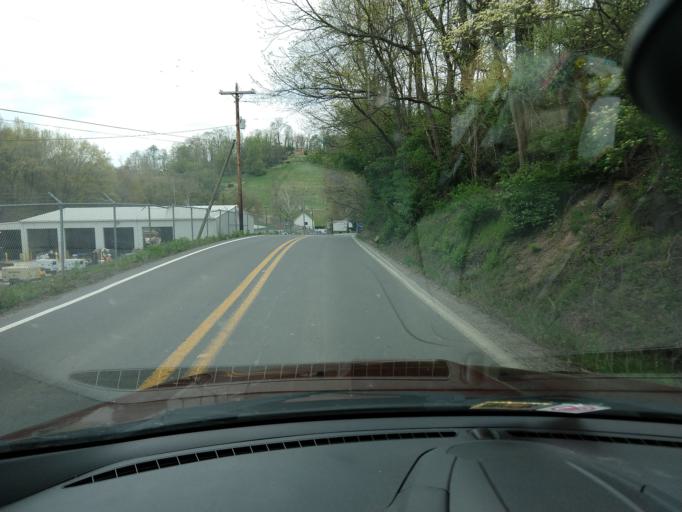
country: US
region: West Virginia
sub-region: Harrison County
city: Despard
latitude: 39.3334
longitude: -80.2876
